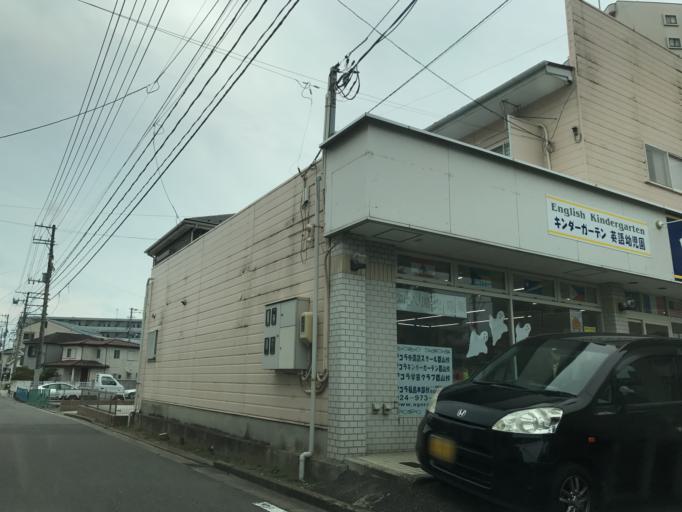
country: JP
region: Fukushima
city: Koriyama
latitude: 37.4036
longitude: 140.3707
